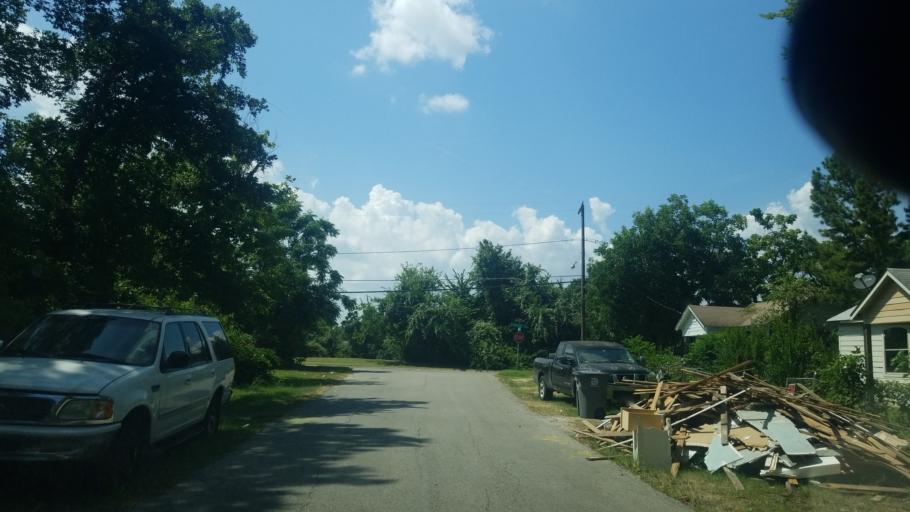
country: US
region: Texas
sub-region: Dallas County
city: Hutchins
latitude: 32.7150
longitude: -96.7467
